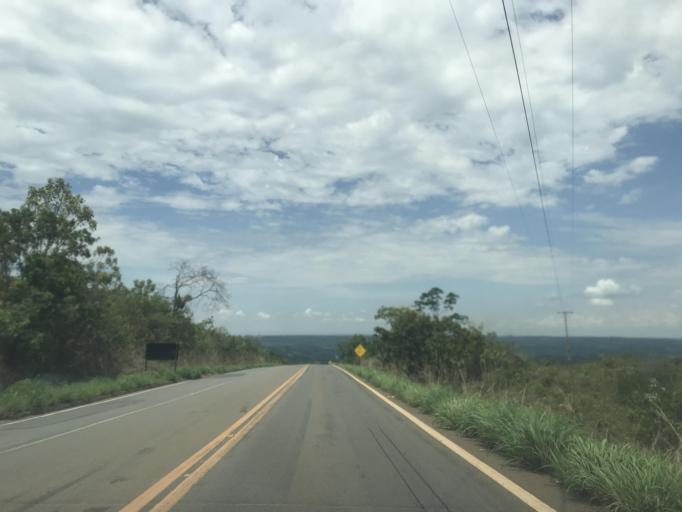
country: BR
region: Goias
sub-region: Luziania
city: Luziania
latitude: -16.3497
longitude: -48.0400
